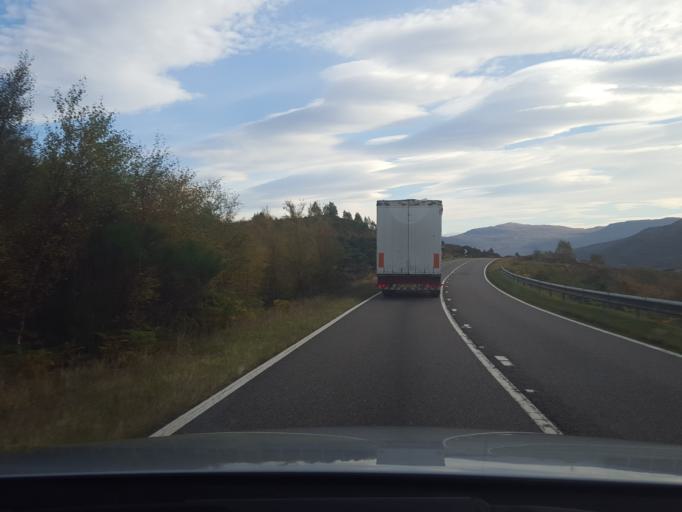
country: GB
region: Scotland
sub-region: Highland
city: Spean Bridge
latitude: 57.1495
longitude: -5.0314
